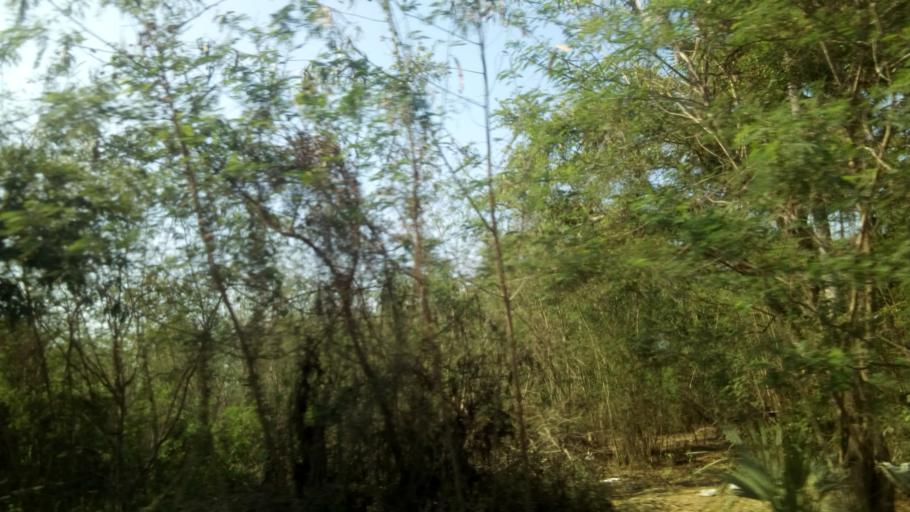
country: TH
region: Nonthaburi
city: Bang Yai
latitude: 13.8799
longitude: 100.3069
